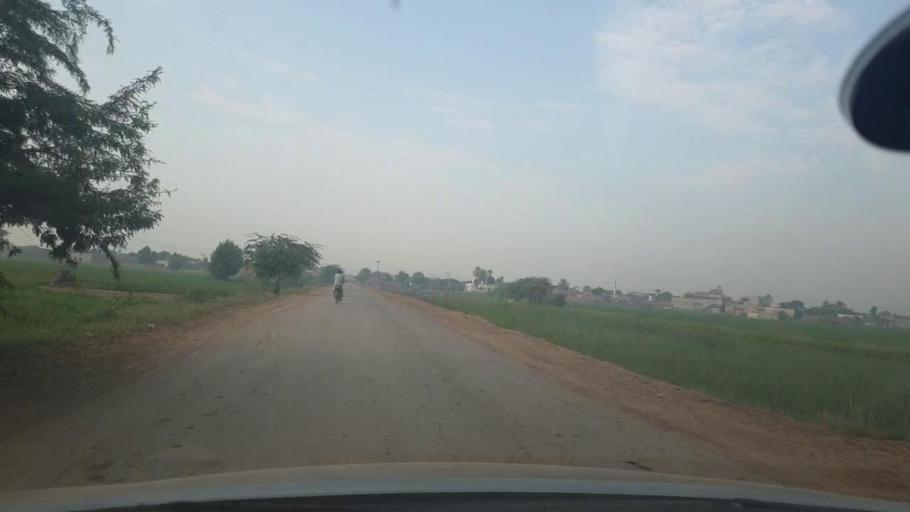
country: PK
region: Sindh
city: Jacobabad
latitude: 28.2714
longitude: 68.4212
